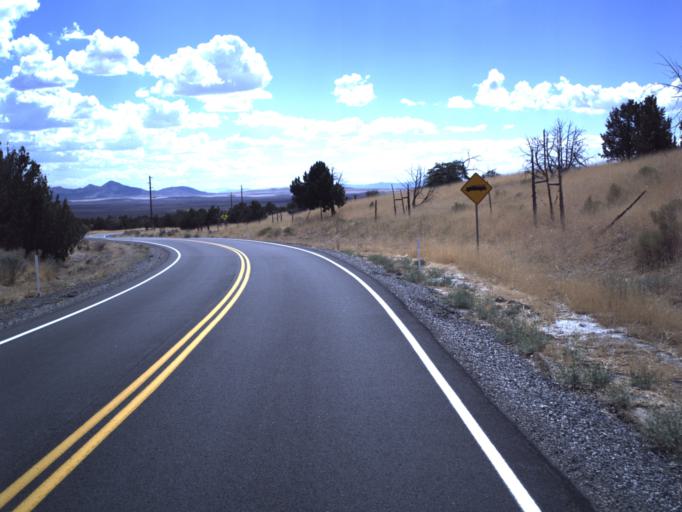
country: US
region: Utah
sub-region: Tooele County
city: Grantsville
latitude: 40.3226
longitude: -112.6261
